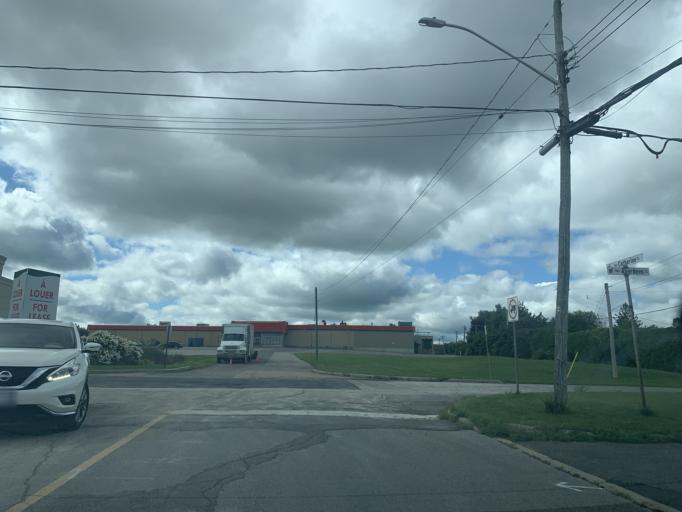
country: CA
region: Ontario
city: Hawkesbury
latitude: 45.6059
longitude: -74.5981
